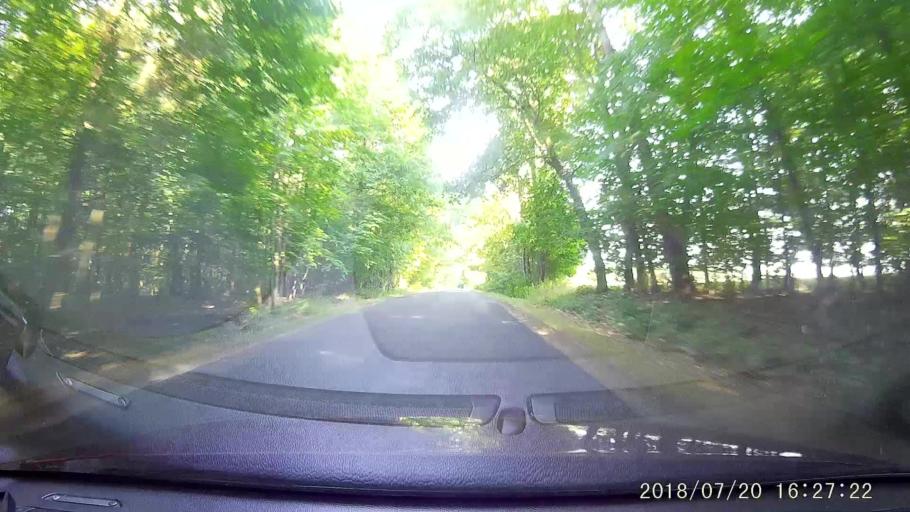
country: PL
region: Lower Silesian Voivodeship
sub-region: Powiat zgorzelecki
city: Lagow
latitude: 51.1259
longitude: 15.0449
